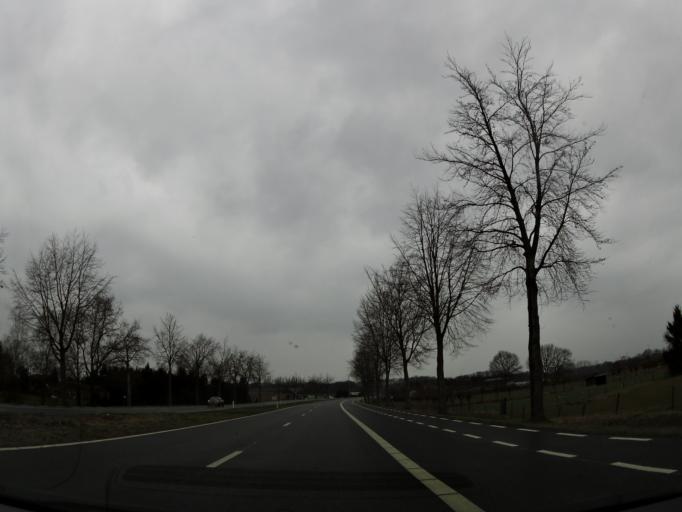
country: BE
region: Flanders
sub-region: Provincie Limburg
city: Maaseik
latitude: 51.0865
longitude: 5.7731
